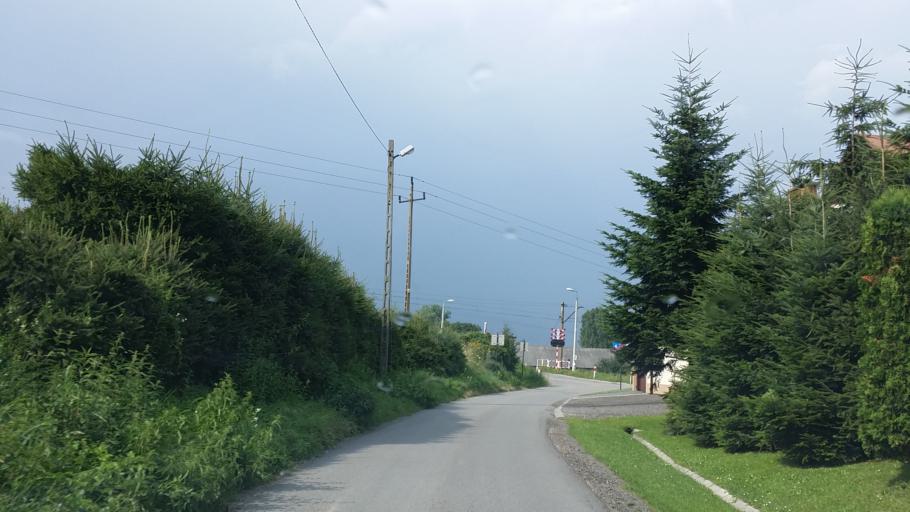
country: PL
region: Lesser Poland Voivodeship
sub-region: Powiat wadowicki
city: Spytkowice
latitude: 50.0002
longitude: 19.5112
